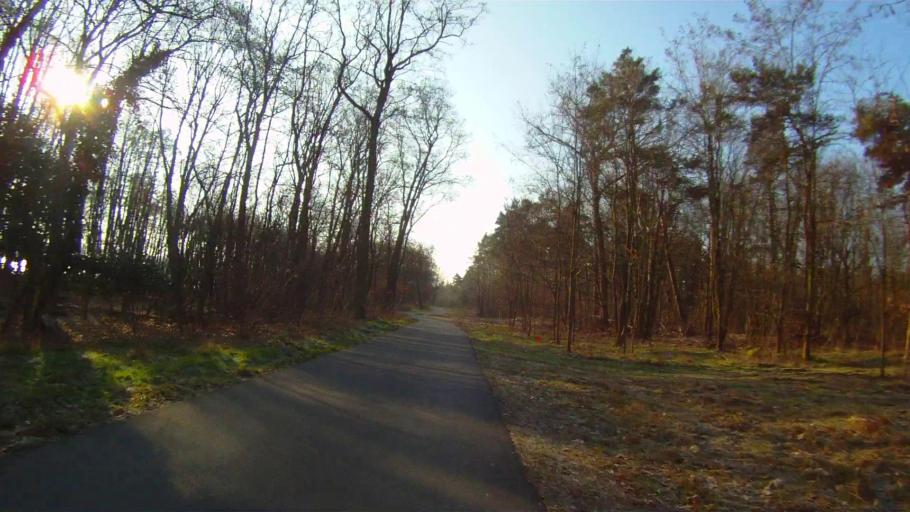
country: DE
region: Berlin
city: Friedrichshagen
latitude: 52.4358
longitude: 13.6196
